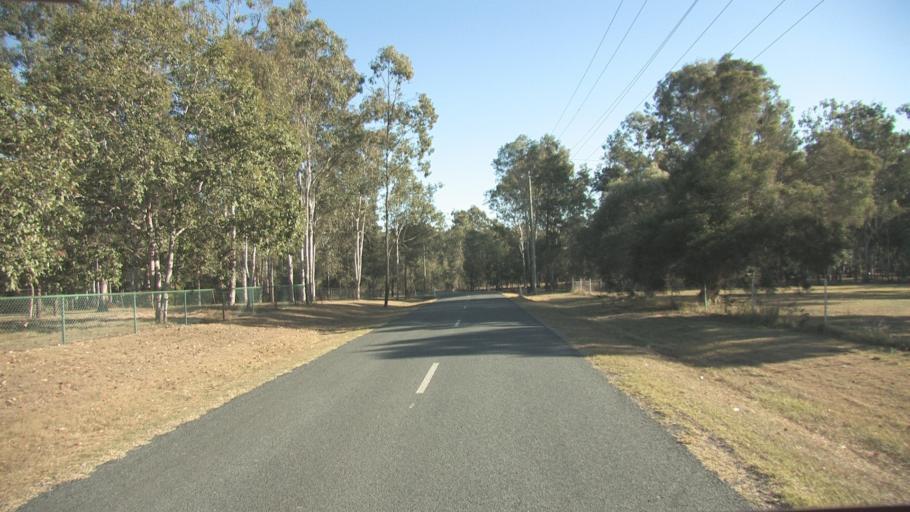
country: AU
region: Queensland
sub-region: Logan
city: North Maclean
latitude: -27.7974
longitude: 152.9926
